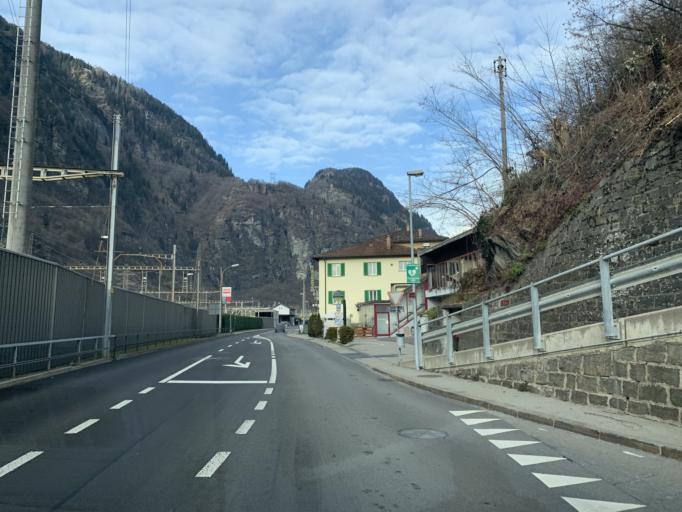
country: CH
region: Ticino
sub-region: Leventina District
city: Faido
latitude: 46.4396
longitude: 8.8426
